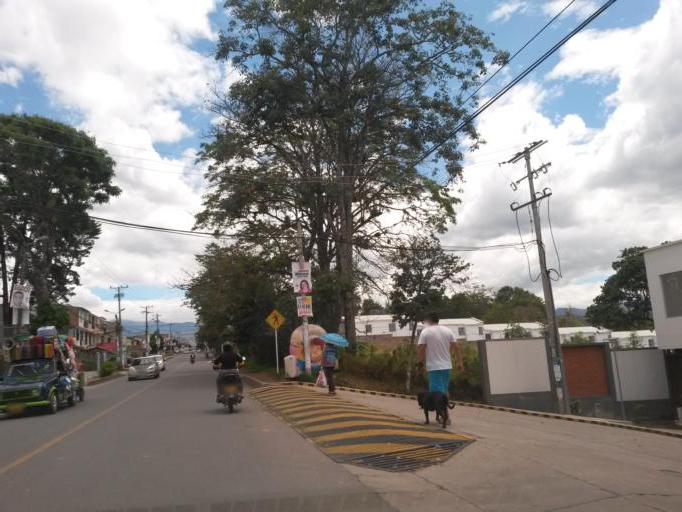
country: CO
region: Cauca
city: Popayan
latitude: 2.4845
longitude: -76.5806
